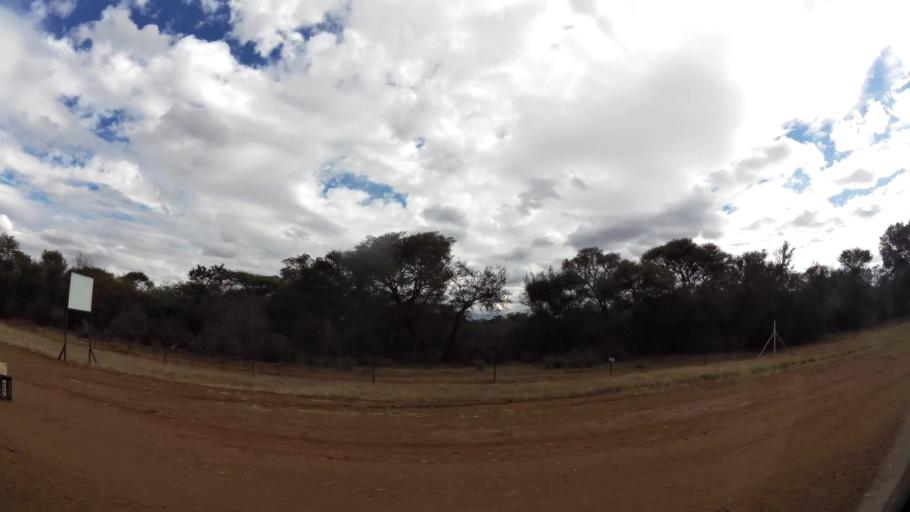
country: ZA
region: Limpopo
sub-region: Waterberg District Municipality
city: Warmbaths
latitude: -24.8980
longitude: 28.2808
